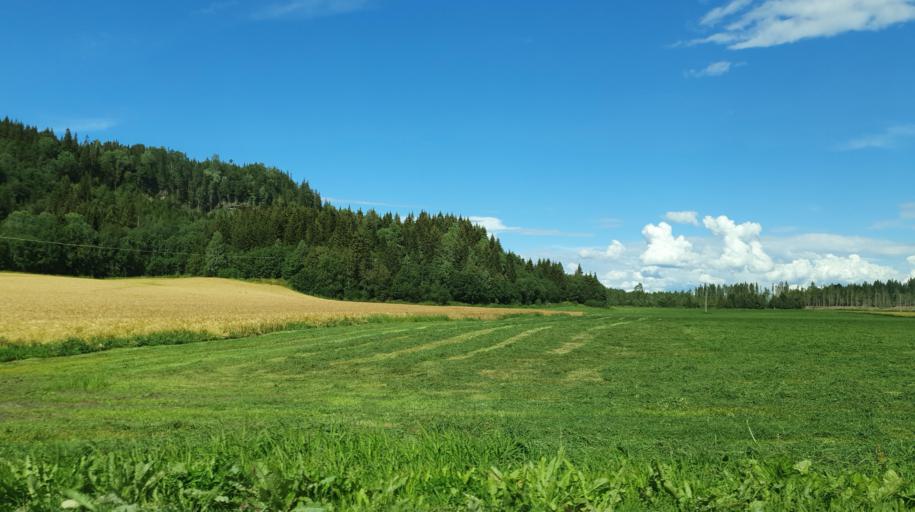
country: NO
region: Nord-Trondelag
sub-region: Levanger
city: Levanger
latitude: 63.6970
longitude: 11.2652
